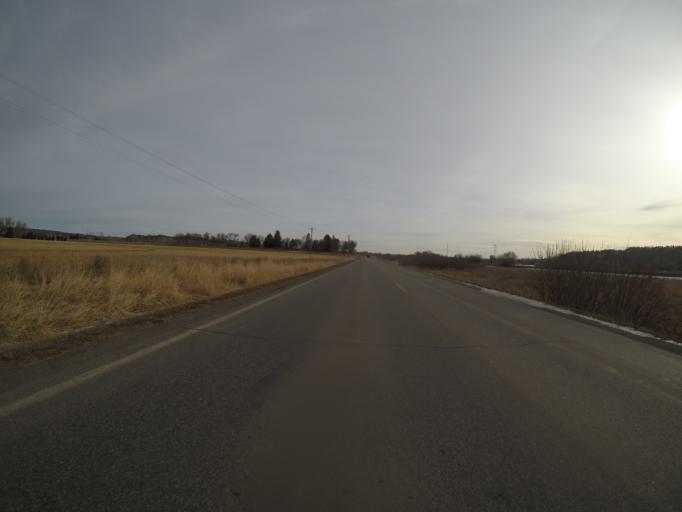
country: US
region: Montana
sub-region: Stillwater County
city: Columbus
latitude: 45.6418
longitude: -109.2782
